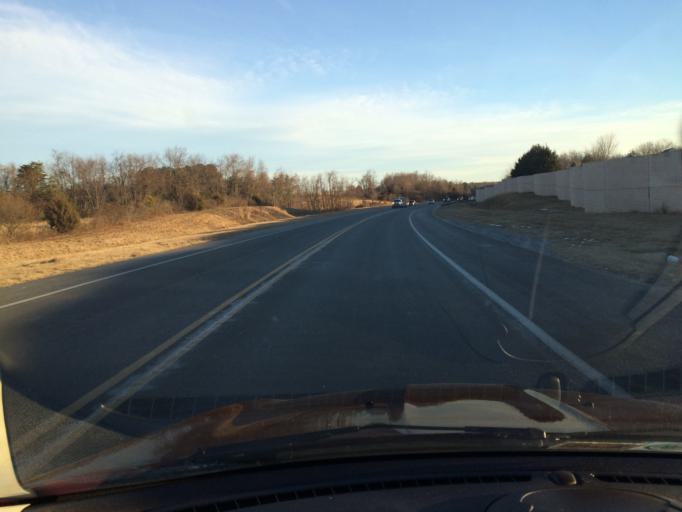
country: US
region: Virginia
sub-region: City of Staunton
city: Staunton
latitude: 38.1716
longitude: -79.1061
